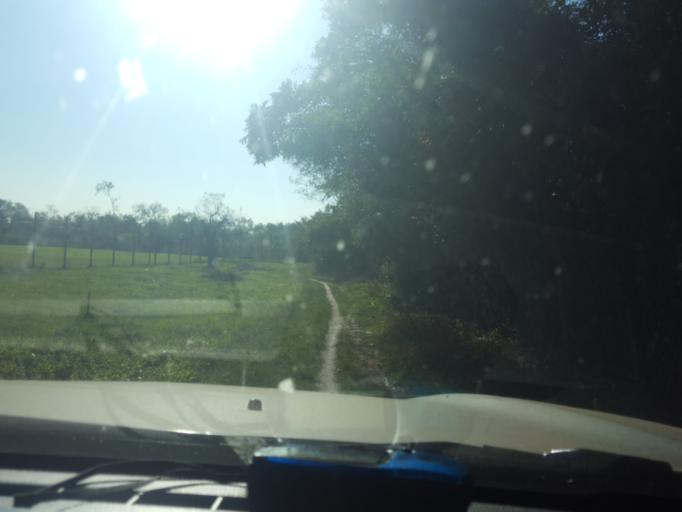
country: PY
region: Cordillera
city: Atyra
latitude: -25.2589
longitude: -57.1170
